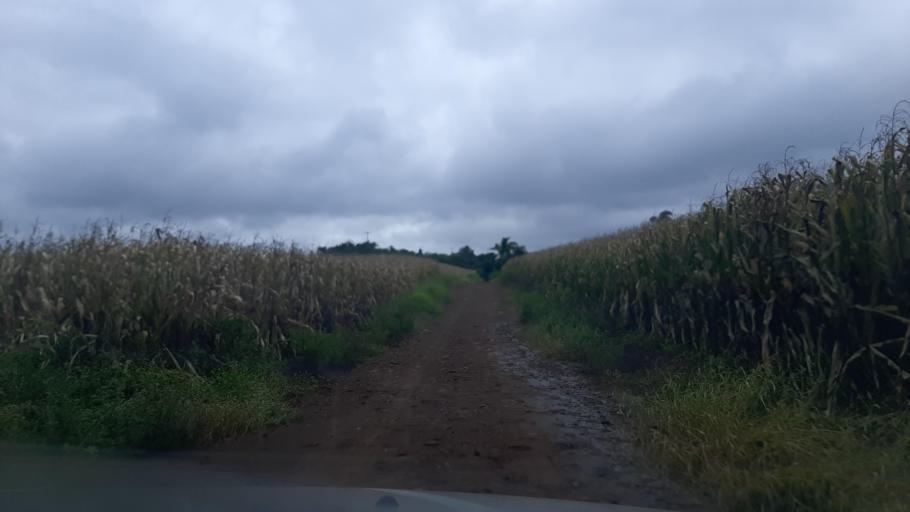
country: BR
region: Parana
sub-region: Ampere
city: Ampere
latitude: -26.0496
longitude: -53.5319
